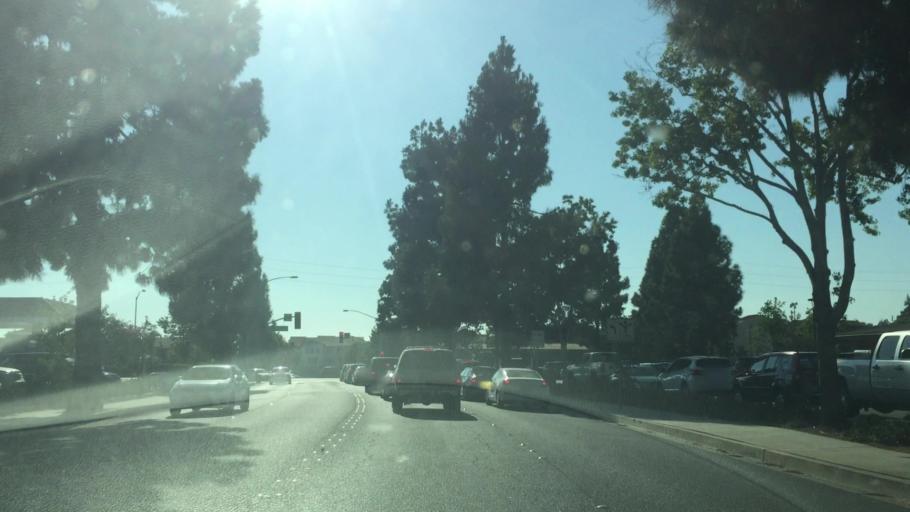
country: US
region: California
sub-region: Ventura County
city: Camarillo
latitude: 34.2218
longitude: -119.0685
